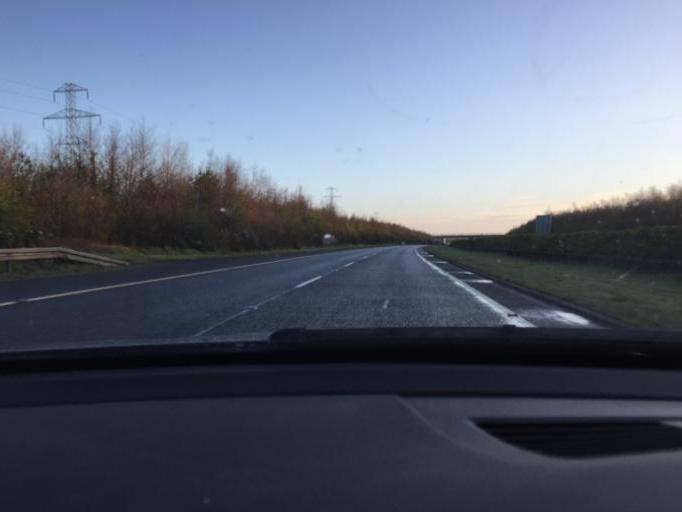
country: IE
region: Leinster
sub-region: Fingal County
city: Swords
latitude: 53.4878
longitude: -6.2060
